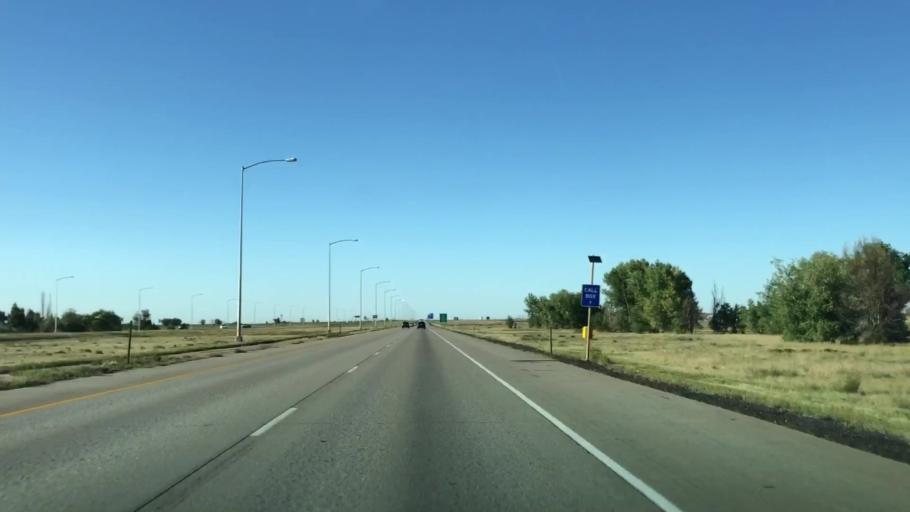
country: US
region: Colorado
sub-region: Adams County
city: Aurora
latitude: 39.8053
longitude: -104.7863
